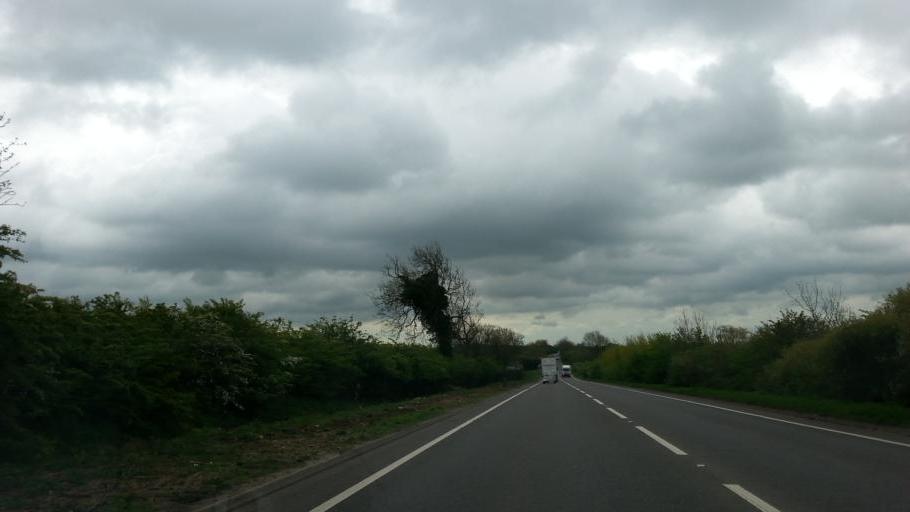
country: GB
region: England
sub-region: Leicestershire
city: Lutterworth
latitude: 52.4180
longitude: -1.2212
